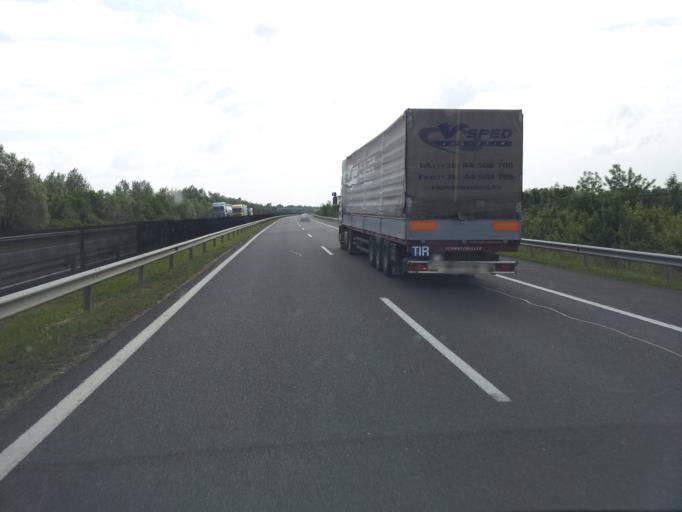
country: HU
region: Borsod-Abauj-Zemplen
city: Hejobaba
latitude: 47.8720
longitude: 20.9623
